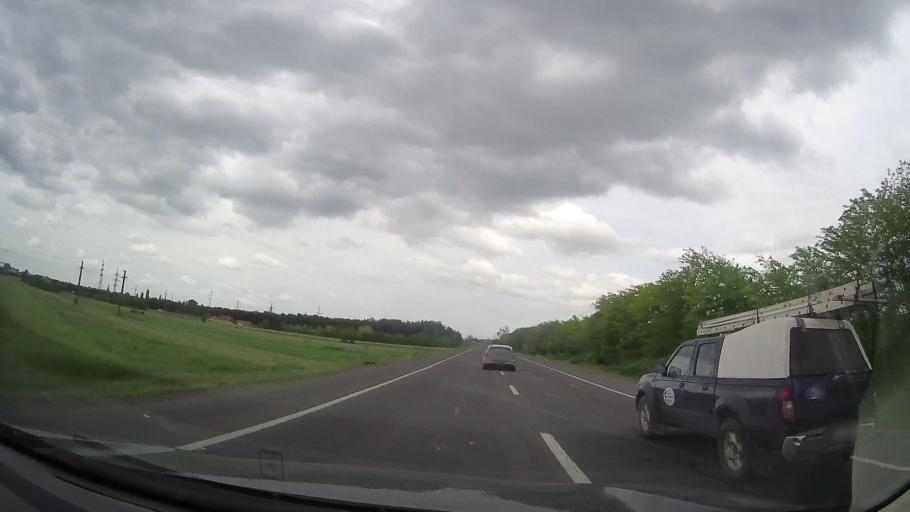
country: RO
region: Dolj
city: Craiova
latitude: 44.3466
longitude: 23.8294
